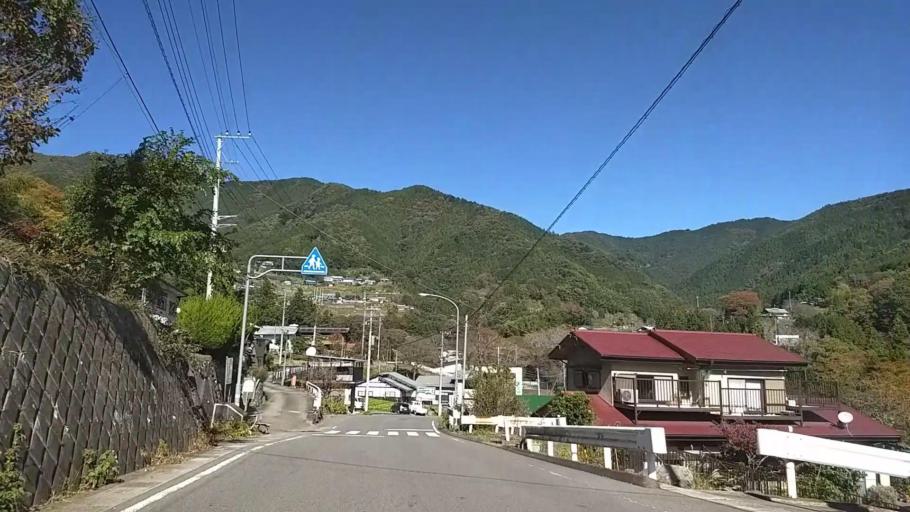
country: JP
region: Yamanashi
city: Uenohara
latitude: 35.6693
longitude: 139.0888
